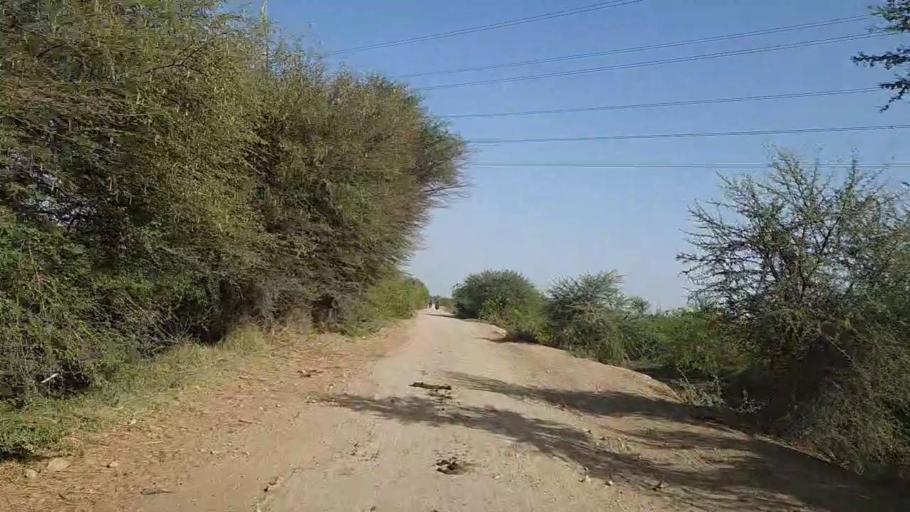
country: PK
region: Sindh
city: Kotri
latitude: 25.1633
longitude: 68.2980
